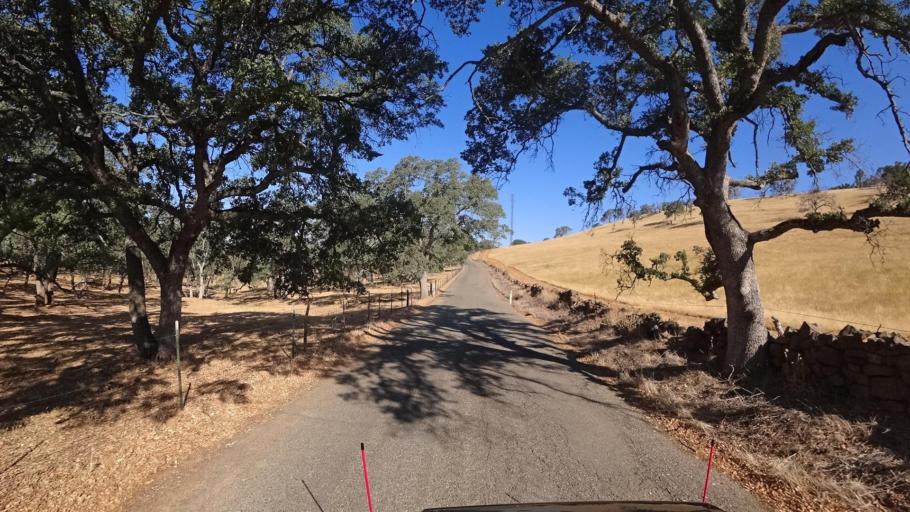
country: US
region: California
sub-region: Mariposa County
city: Mariposa
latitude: 37.5885
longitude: -120.1806
